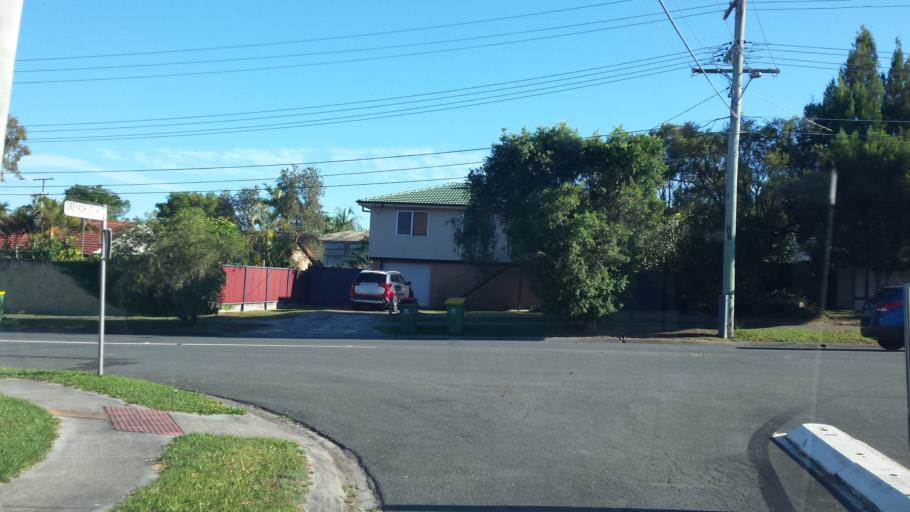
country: AU
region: Queensland
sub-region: Logan
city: Logan City
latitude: -27.6521
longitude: 153.1008
